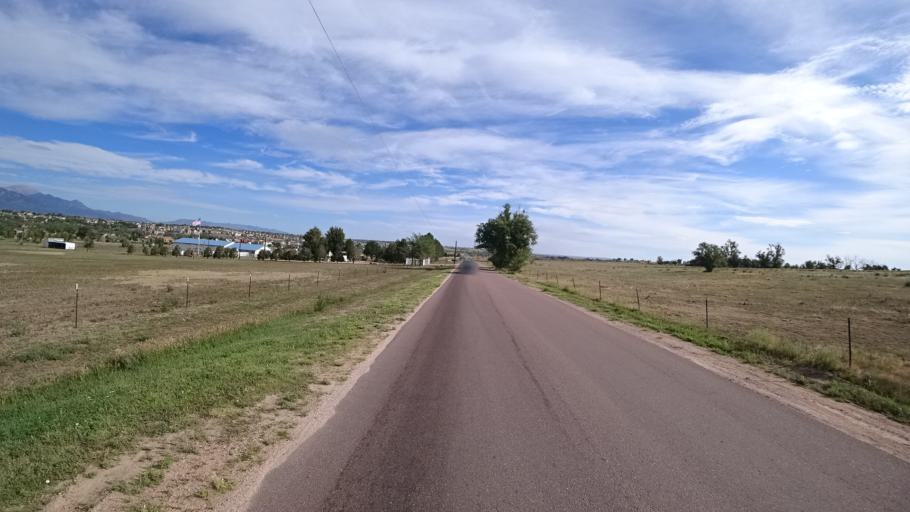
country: US
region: Colorado
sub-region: El Paso County
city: Fountain
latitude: 38.6846
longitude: -104.6782
